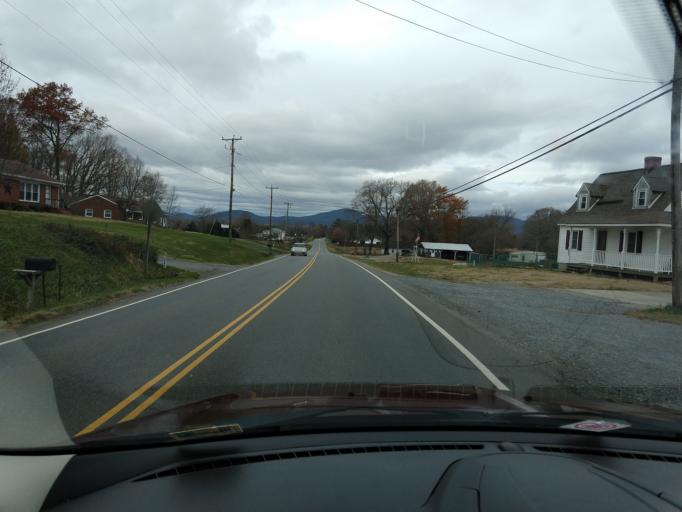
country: US
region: Virginia
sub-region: Botetourt County
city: Blue Ridge
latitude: 37.2593
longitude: -79.7270
